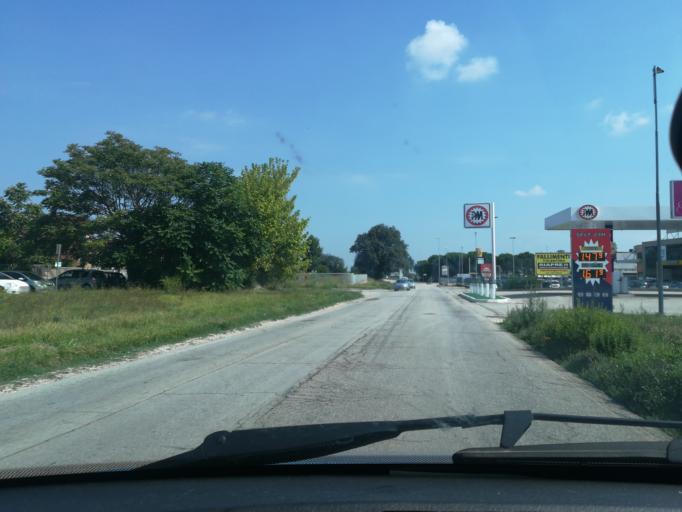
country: IT
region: The Marches
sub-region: Provincia di Macerata
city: Tolentino
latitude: 43.2217
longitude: 13.3303
